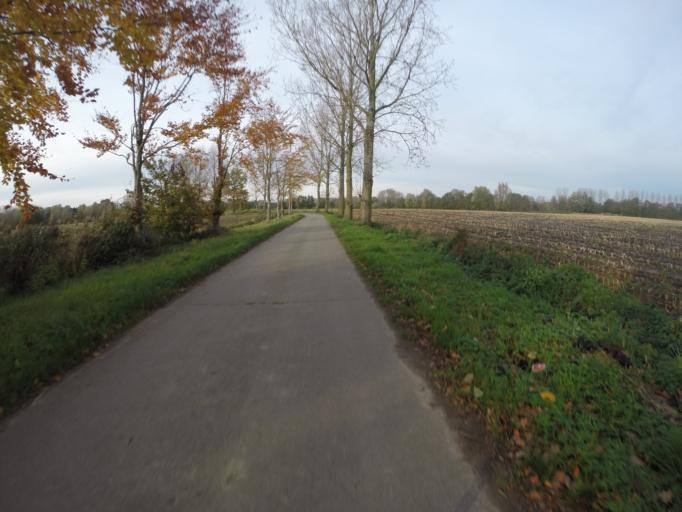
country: BE
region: Flanders
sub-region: Provincie Oost-Vlaanderen
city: Nevele
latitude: 51.0646
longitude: 3.5120
